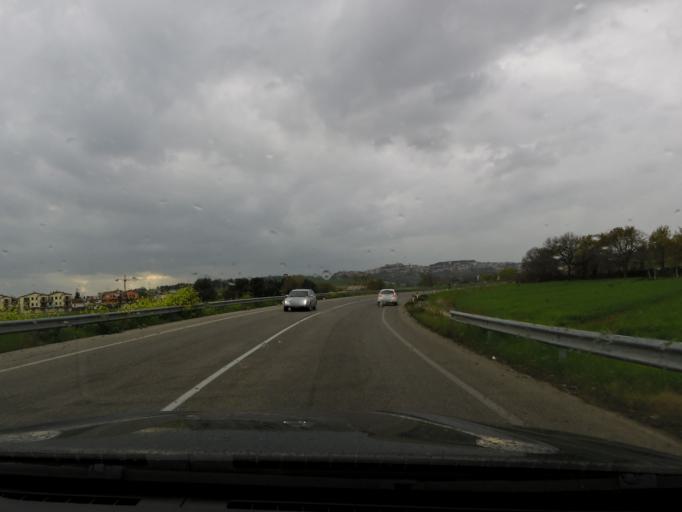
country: IT
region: The Marches
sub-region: Provincia di Ancona
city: Villa Musone
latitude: 43.4564
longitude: 13.5914
